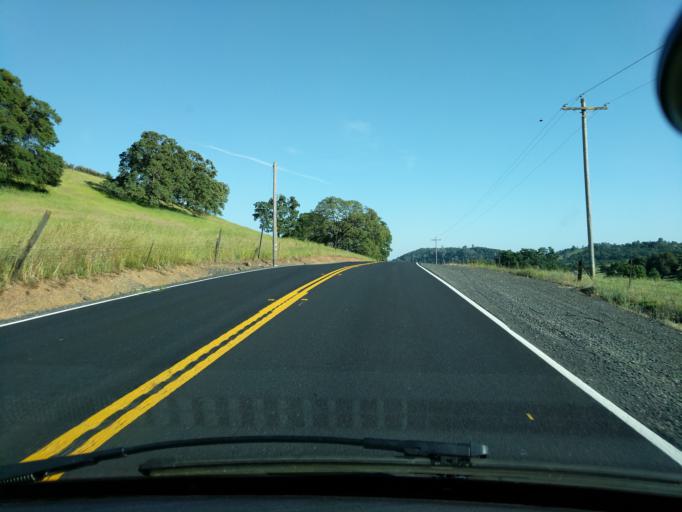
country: US
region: California
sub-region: Calaveras County
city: Copperopolis
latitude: 38.0254
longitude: -120.6454
